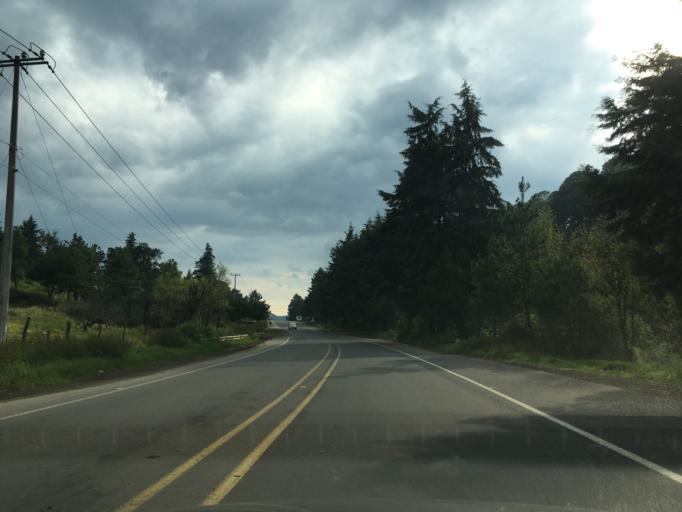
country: MX
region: Michoacan
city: Capacuaro
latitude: 19.5198
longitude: -102.1120
